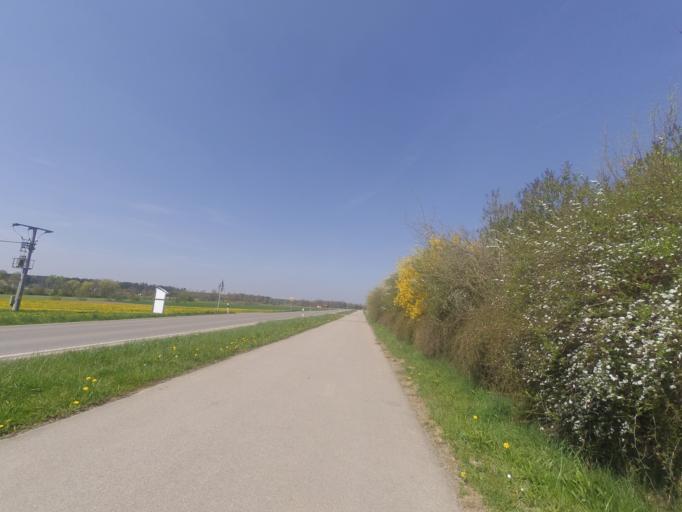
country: DE
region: Bavaria
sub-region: Swabia
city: Weissenhorn
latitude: 48.2801
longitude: 10.1638
